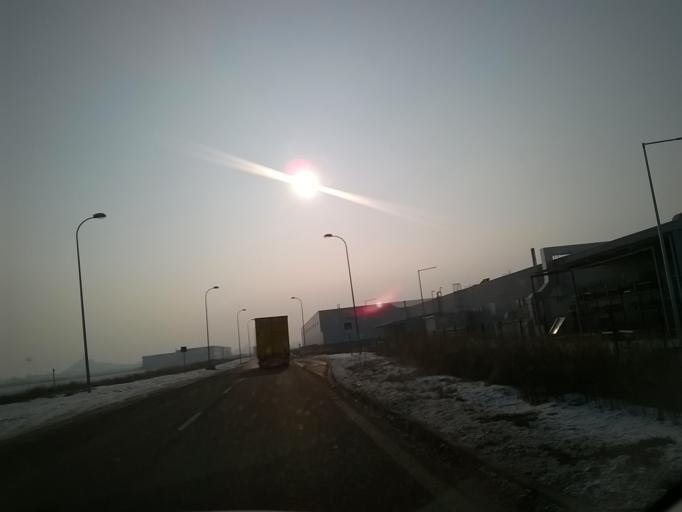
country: SK
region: Nitriansky
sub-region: Okres Nitra
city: Nitra
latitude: 48.3335
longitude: 18.0555
